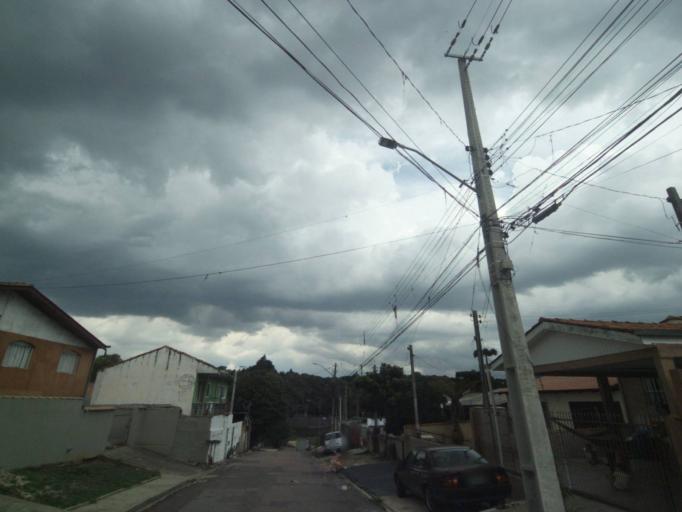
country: BR
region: Parana
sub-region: Curitiba
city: Curitiba
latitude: -25.4564
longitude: -49.3430
